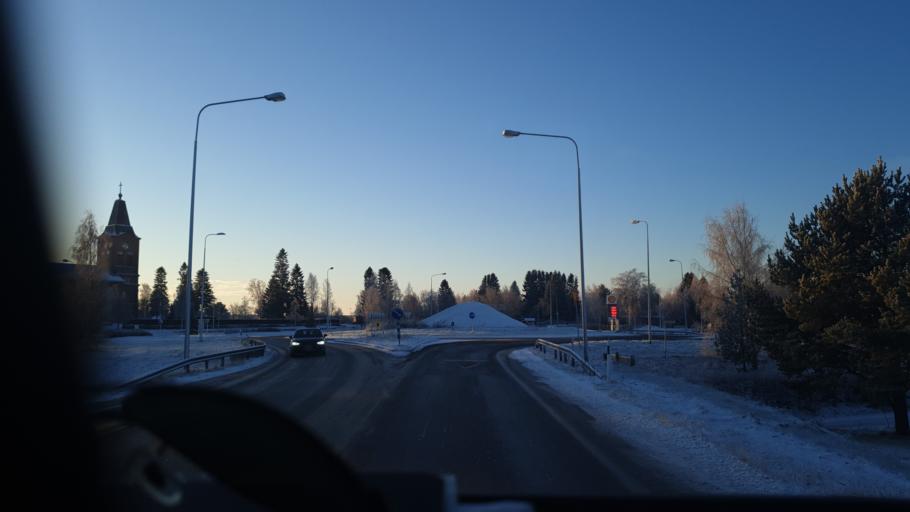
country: FI
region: Northern Ostrobothnia
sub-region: Ylivieska
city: Kalajoki
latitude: 64.2563
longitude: 23.9384
